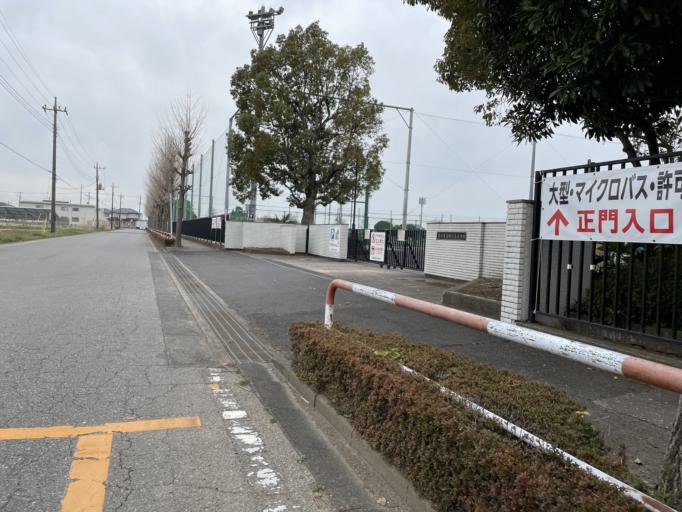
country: JP
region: Saitama
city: Kisai
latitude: 36.1066
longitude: 139.5667
